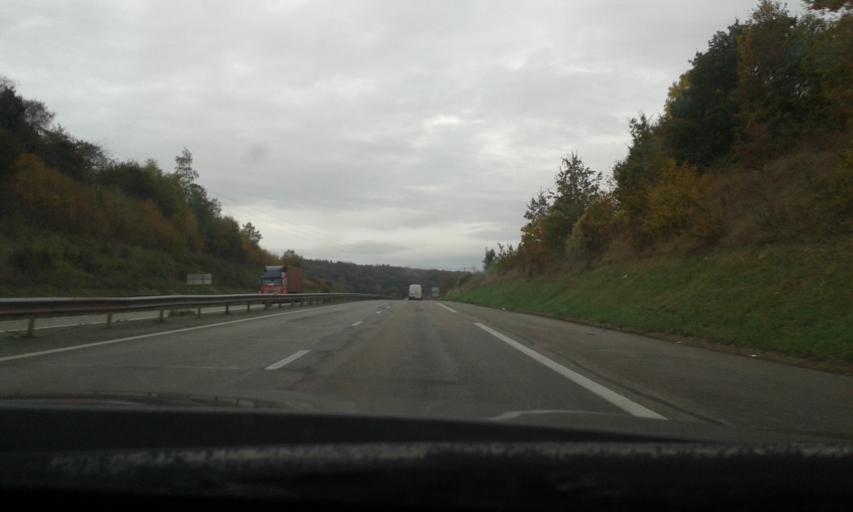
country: FR
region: Haute-Normandie
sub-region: Departement de l'Eure
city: Acquigny
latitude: 49.1648
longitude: 1.1761
